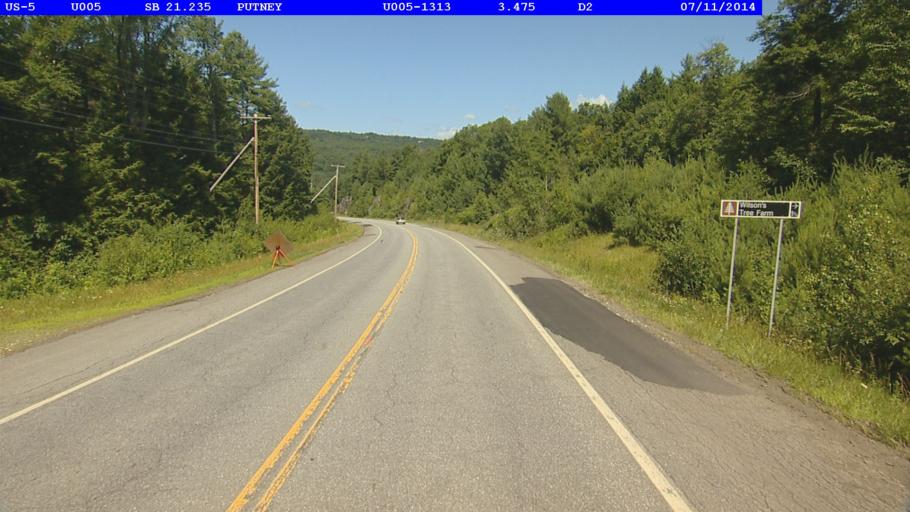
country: US
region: New Hampshire
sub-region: Cheshire County
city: Westmoreland
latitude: 42.9987
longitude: -72.4834
